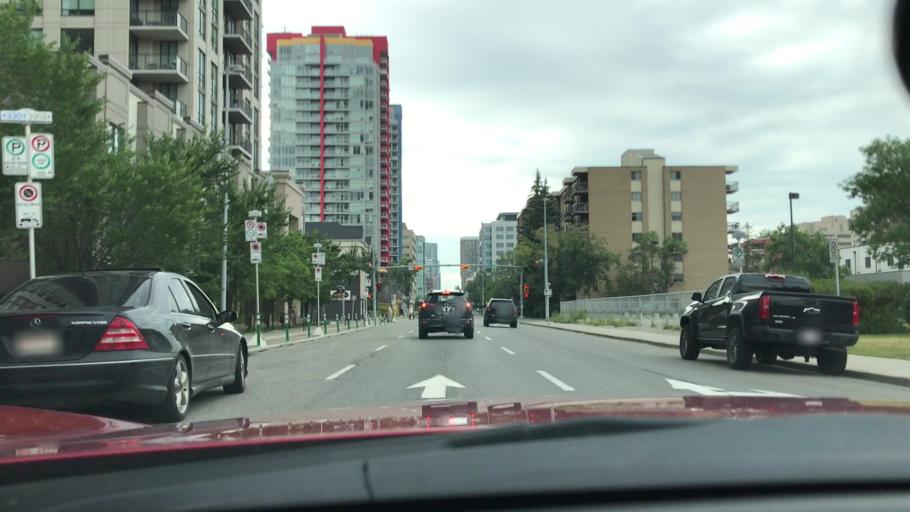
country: CA
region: Alberta
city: Calgary
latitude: 51.0421
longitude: -114.0878
